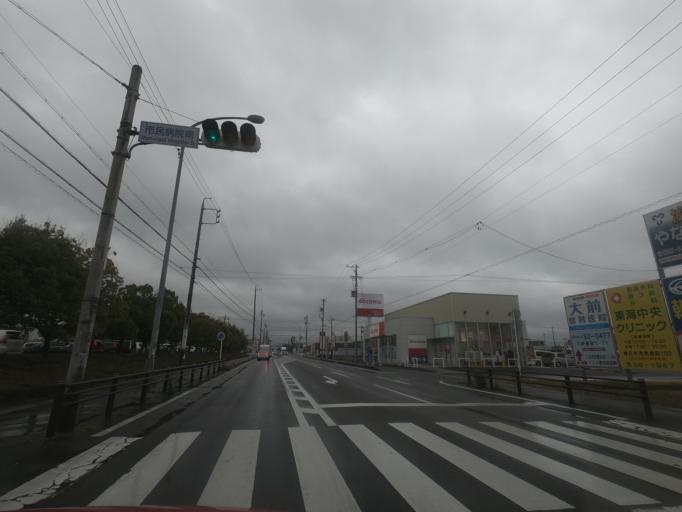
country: JP
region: Aichi
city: Kasugai
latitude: 35.2703
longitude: 136.9705
